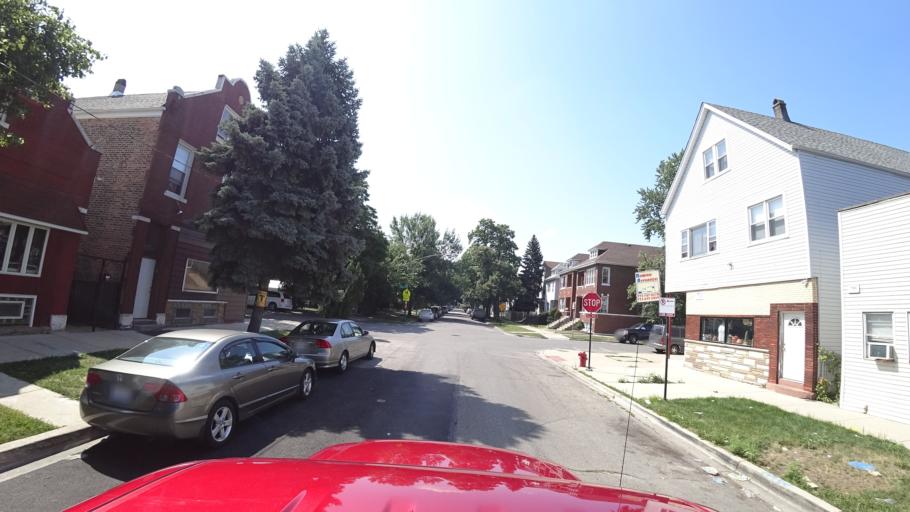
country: US
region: Illinois
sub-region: Cook County
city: Chicago
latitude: 41.8141
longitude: -87.6883
